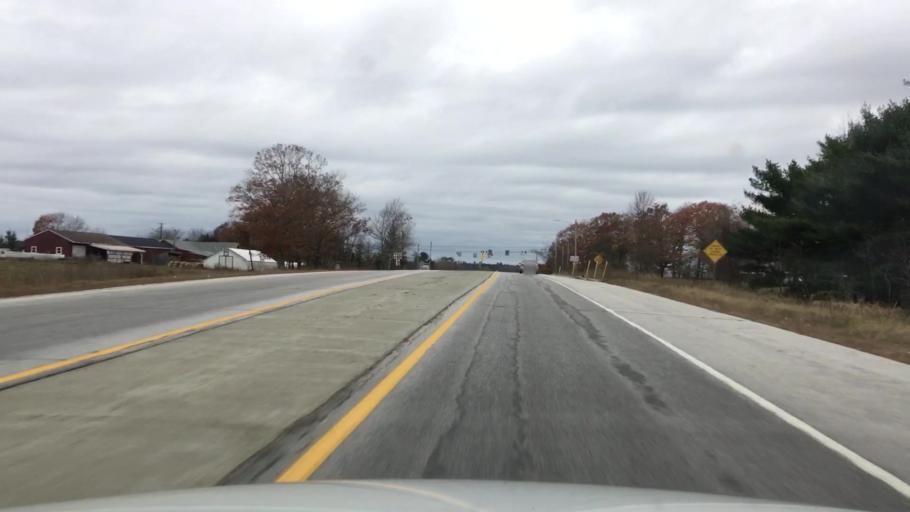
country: US
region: Maine
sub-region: Hancock County
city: Orland
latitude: 44.5726
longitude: -68.7290
